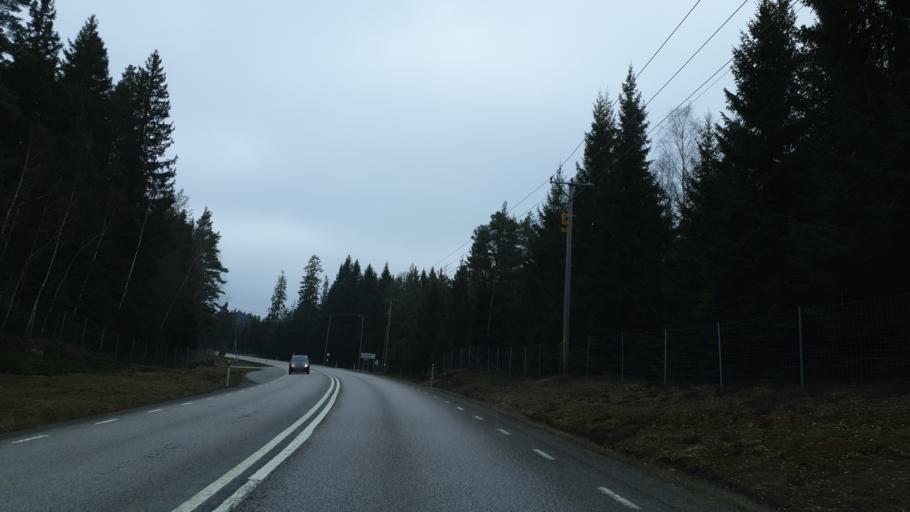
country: SE
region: Vaestra Goetaland
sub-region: Harryda Kommun
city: Hindas
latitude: 57.6453
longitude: 12.4059
